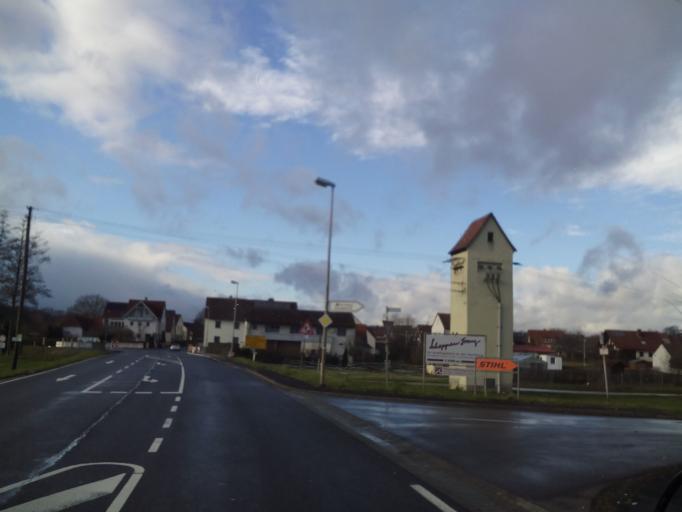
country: DE
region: Bavaria
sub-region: Regierungsbezirk Unterfranken
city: Gossenheim
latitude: 50.0158
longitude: 9.7857
